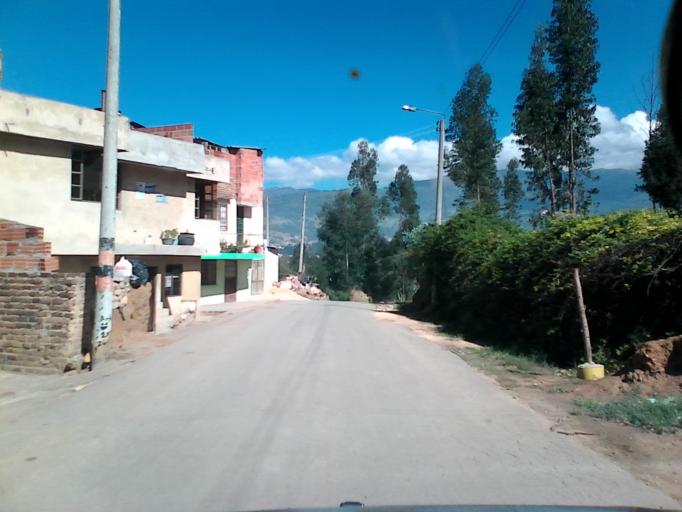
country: CO
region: Boyaca
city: Duitama
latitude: 5.7983
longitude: -73.0142
